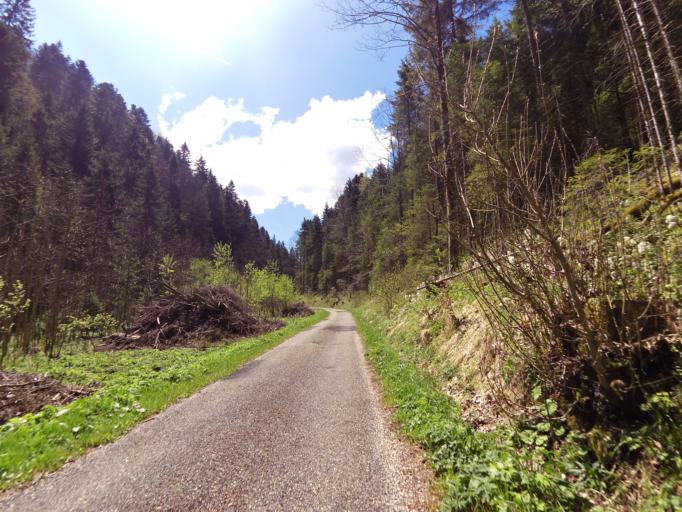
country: CH
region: Vaud
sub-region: Jura-Nord vaudois District
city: L'Abbaye
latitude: 46.6850
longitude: 6.3413
